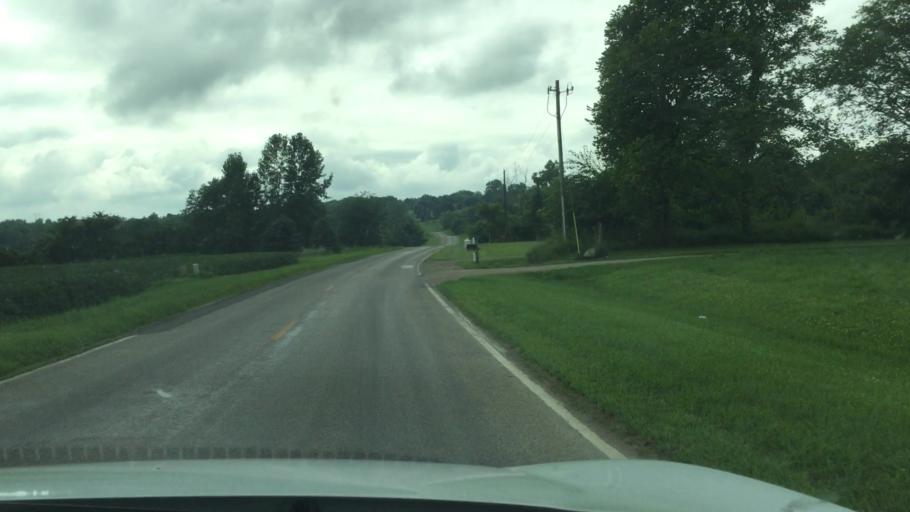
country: US
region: Ohio
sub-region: Champaign County
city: Mechanicsburg
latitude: 40.0594
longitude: -83.6252
